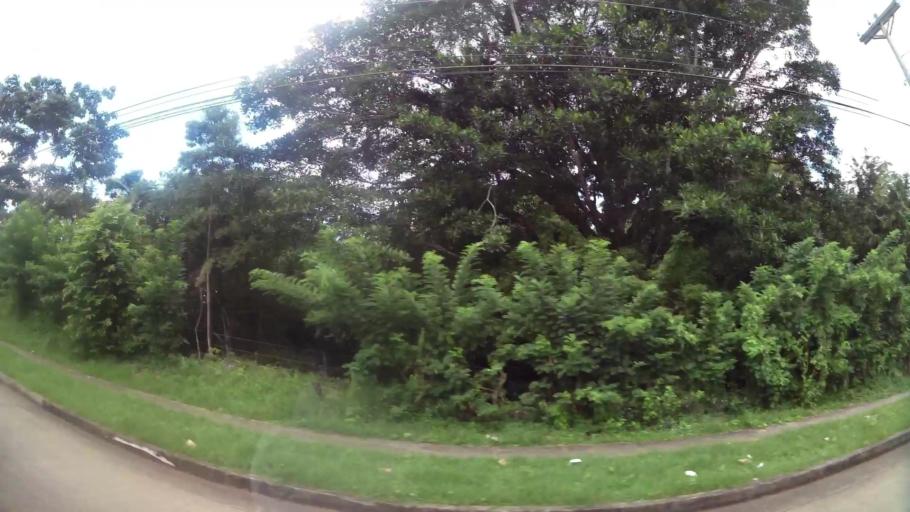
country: PA
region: Panama
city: Nuevo Arraijan
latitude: 8.9267
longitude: -79.7373
